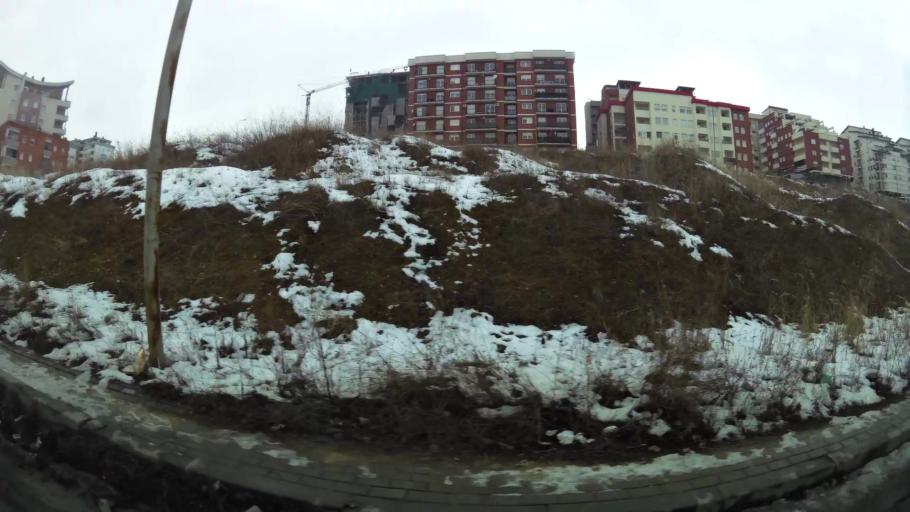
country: XK
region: Pristina
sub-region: Komuna e Prishtines
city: Pristina
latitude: 42.6588
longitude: 21.1497
